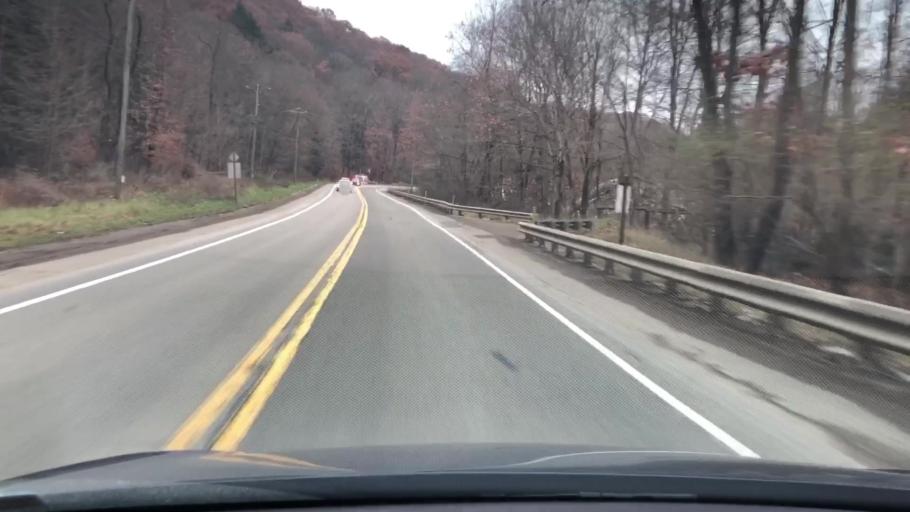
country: US
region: Pennsylvania
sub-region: Clarion County
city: Clarion
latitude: 40.9942
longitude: -79.3422
